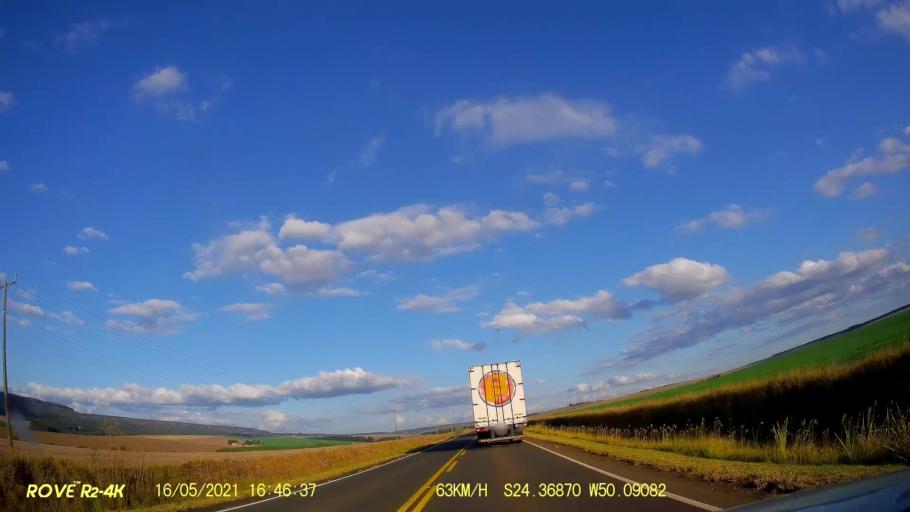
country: BR
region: Parana
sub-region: Pirai Do Sul
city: Pirai do Sul
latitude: -24.3688
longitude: -50.0908
